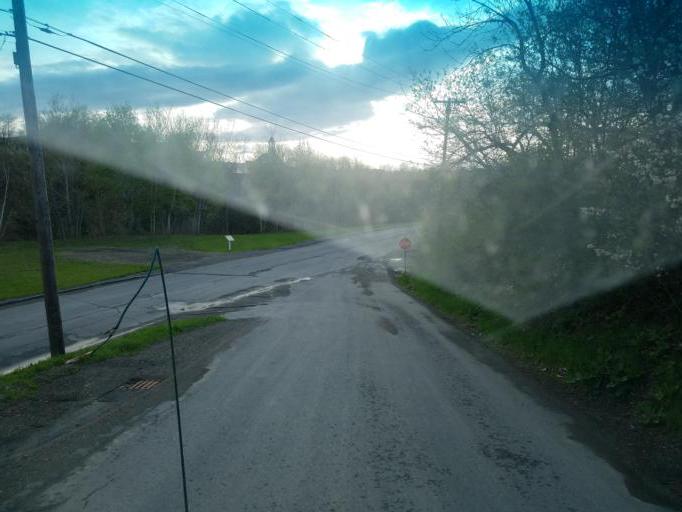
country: US
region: Maine
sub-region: Aroostook County
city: Caribou
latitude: 46.8586
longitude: -68.0080
